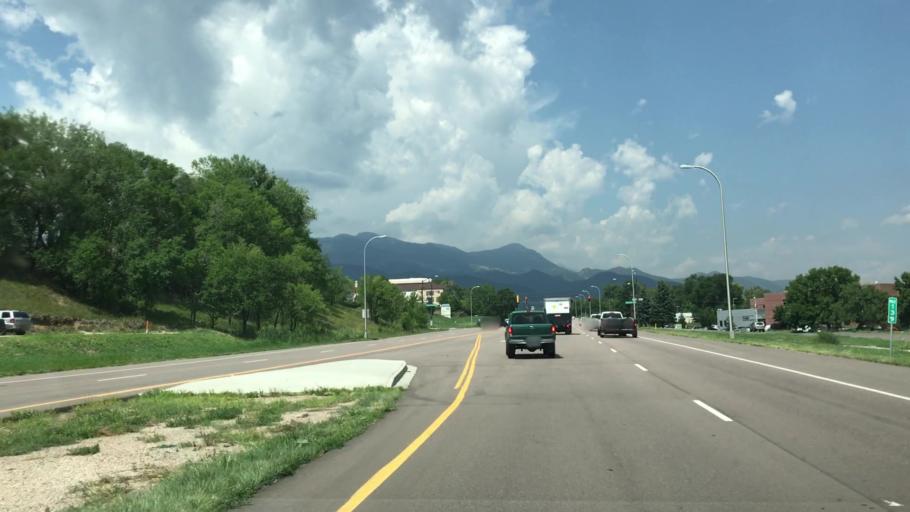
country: US
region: Colorado
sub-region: El Paso County
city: Stratmoor
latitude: 38.7960
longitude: -104.8091
